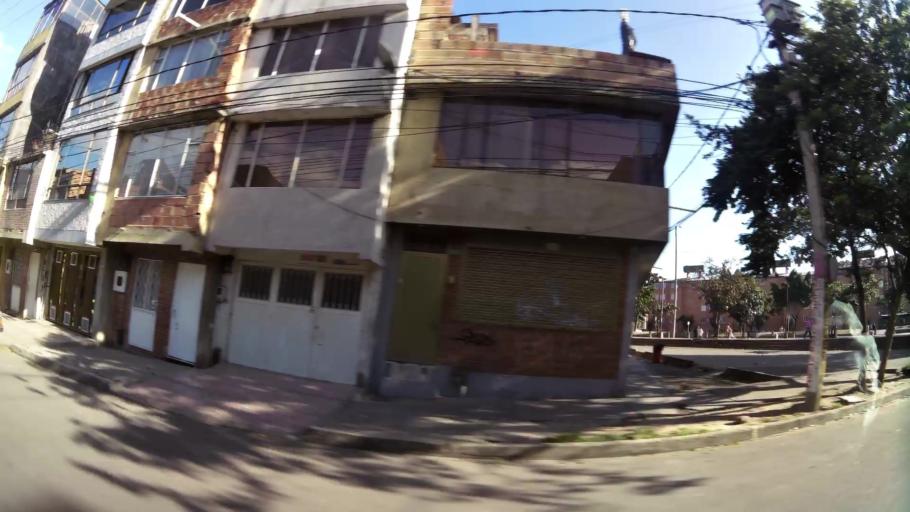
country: CO
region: Cundinamarca
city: Soacha
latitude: 4.5736
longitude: -74.1523
